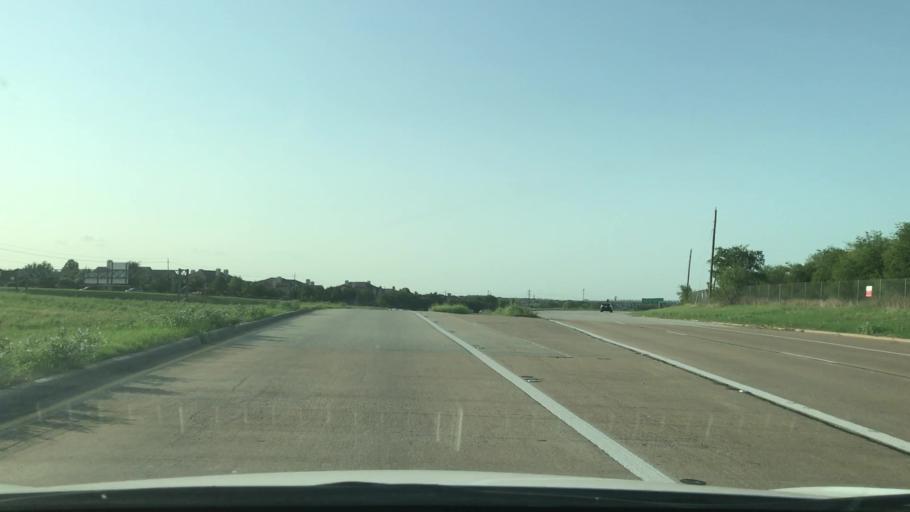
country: US
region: Texas
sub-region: Tarrant County
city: Euless
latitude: 32.8536
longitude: -97.0633
